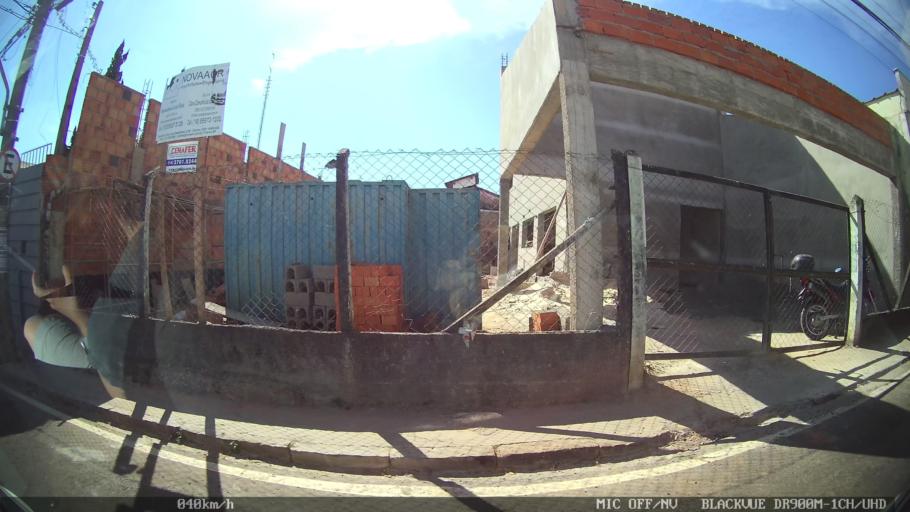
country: BR
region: Sao Paulo
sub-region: Franca
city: Franca
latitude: -20.5342
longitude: -47.4033
